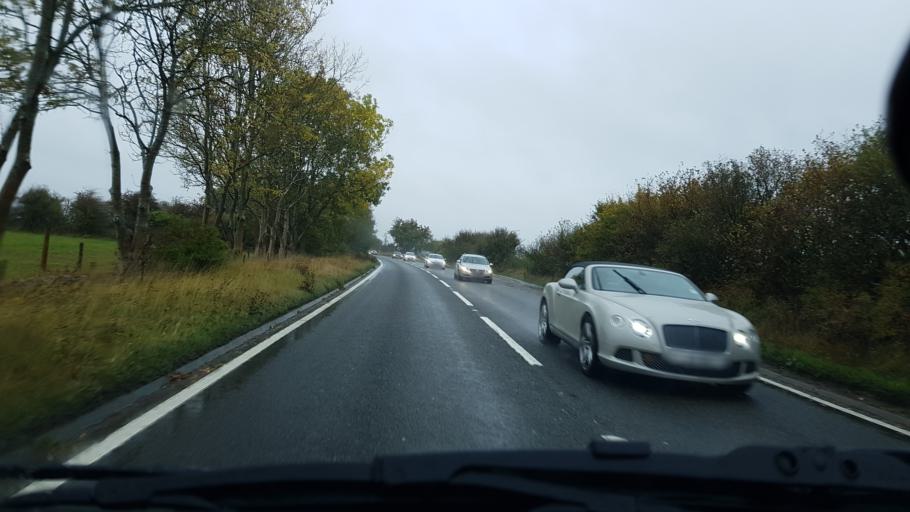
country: GB
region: England
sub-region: Oxfordshire
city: Burford
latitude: 51.7959
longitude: -1.6060
